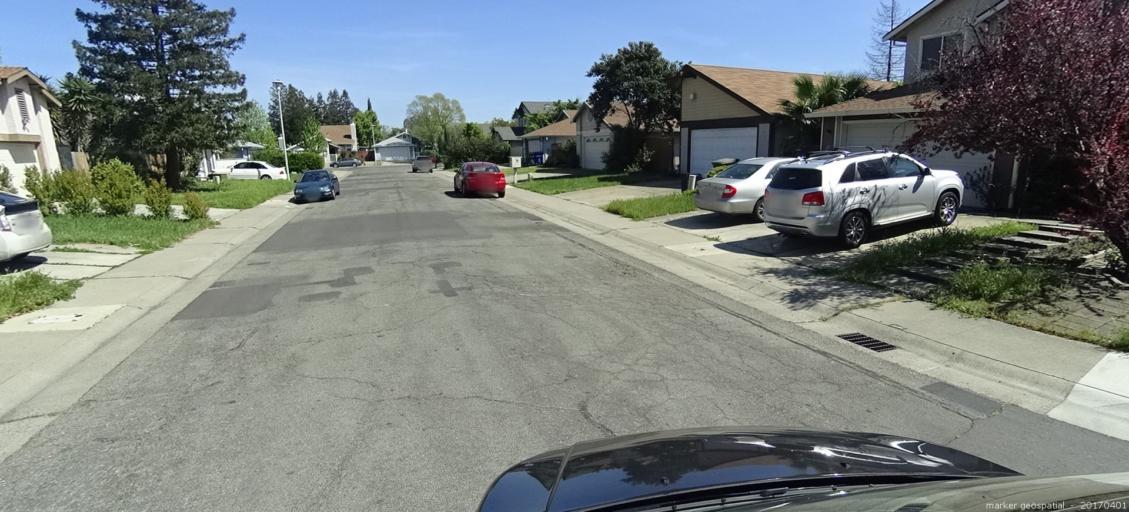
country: US
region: California
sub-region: Sacramento County
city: Laguna
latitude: 38.4495
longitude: -121.4309
